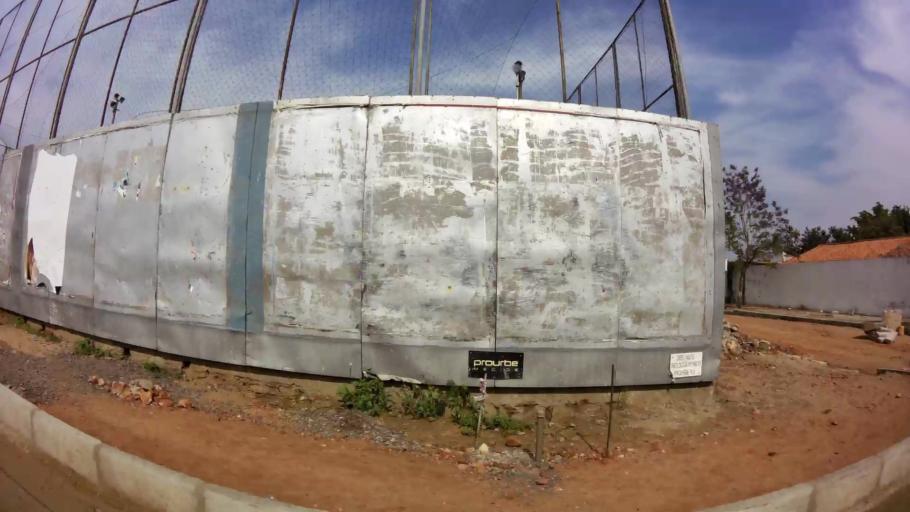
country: PY
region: Central
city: Fernando de la Mora
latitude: -25.2744
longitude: -57.5454
